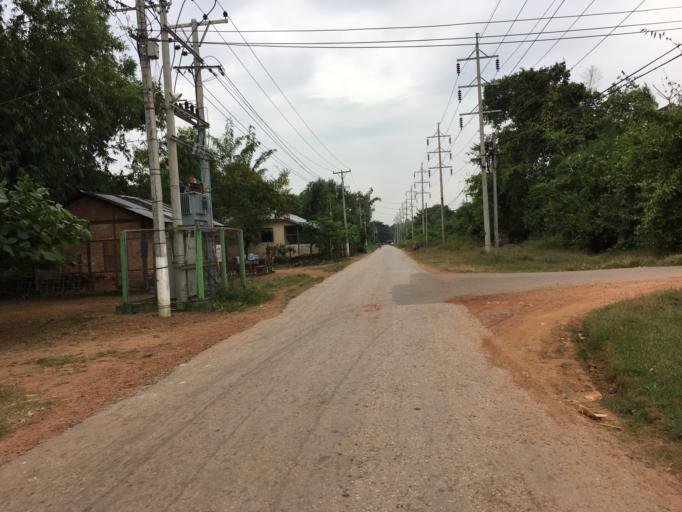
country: MM
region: Mon
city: Mawlamyine
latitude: 16.4283
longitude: 97.6287
